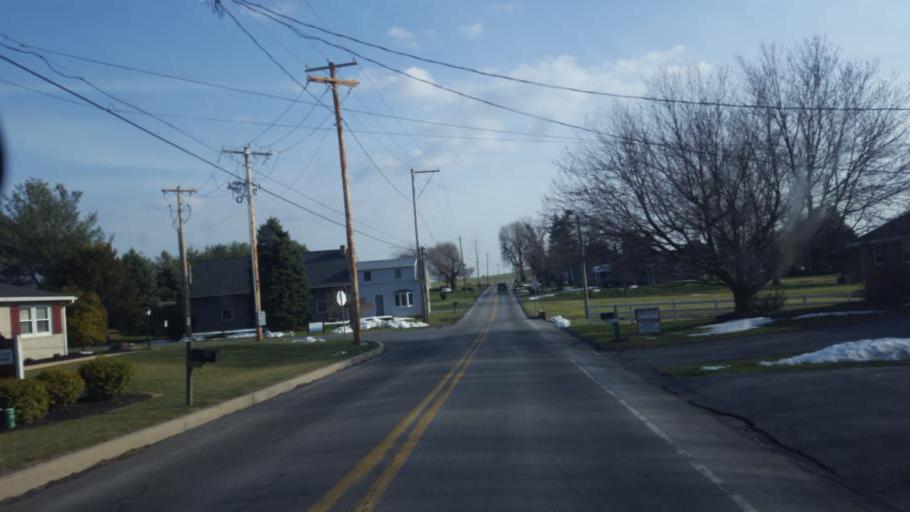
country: US
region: Pennsylvania
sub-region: Lancaster County
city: Brownstown
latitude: 40.0836
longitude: -76.2238
